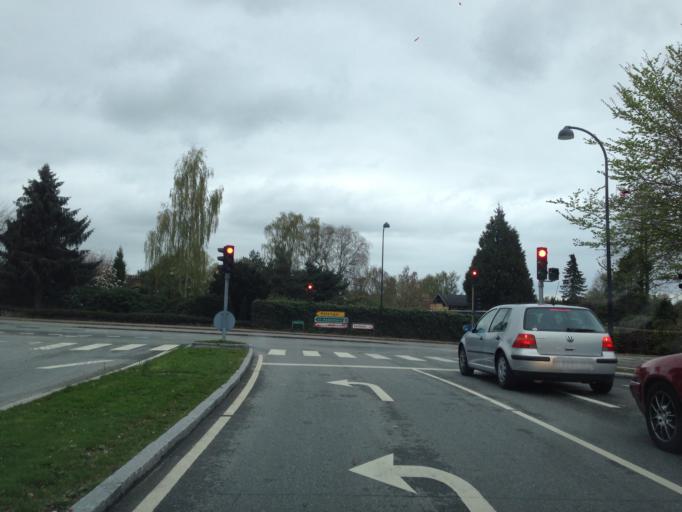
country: DK
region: Capital Region
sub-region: Rudersdal Kommune
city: Trorod
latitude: 55.8458
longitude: 12.5332
